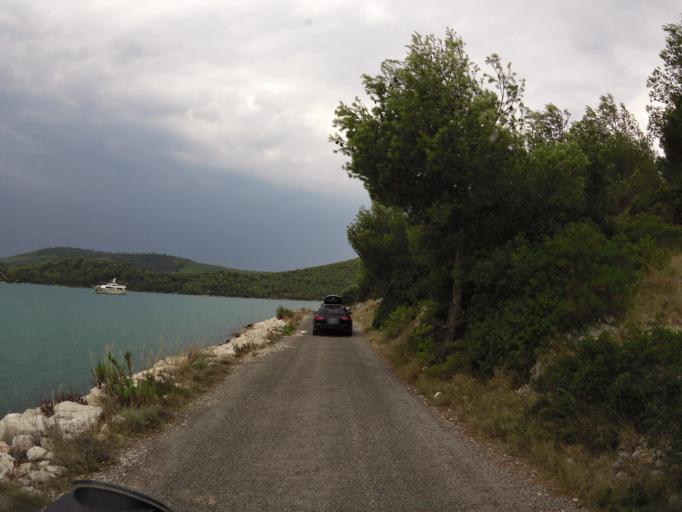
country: HR
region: Zadarska
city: Sali
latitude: 43.9242
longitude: 15.1330
